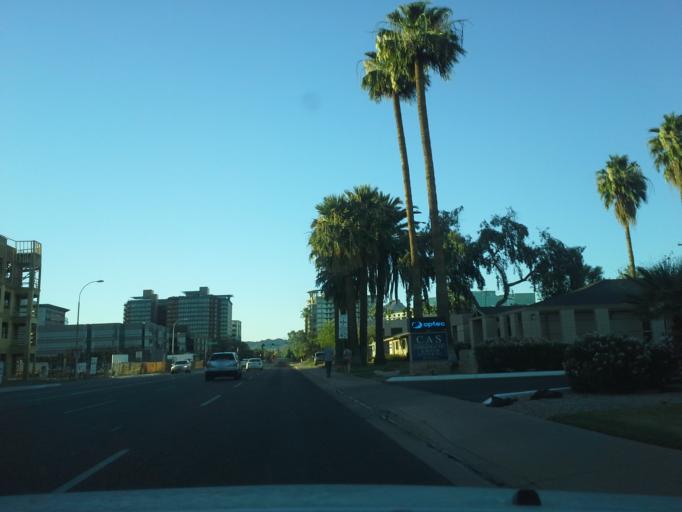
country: US
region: Arizona
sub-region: Maricopa County
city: Phoenix
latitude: 33.5036
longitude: -112.0301
